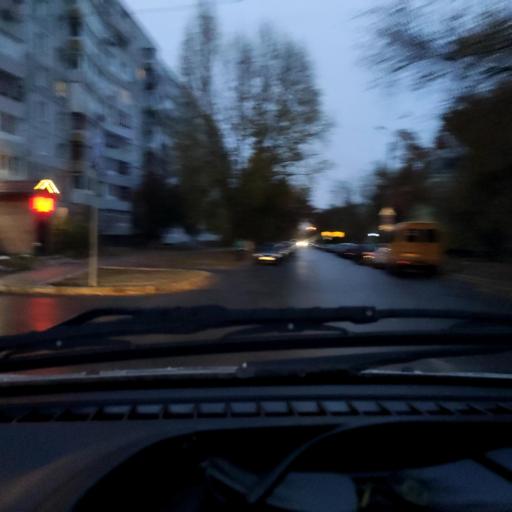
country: RU
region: Samara
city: Zhigulevsk
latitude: 53.4764
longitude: 49.4767
